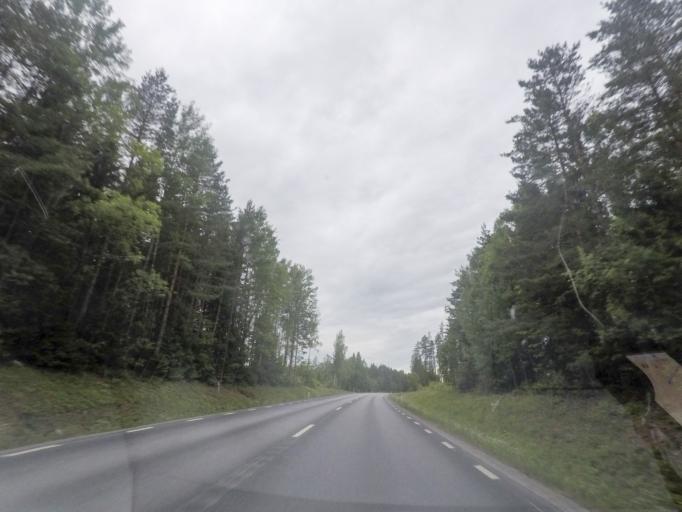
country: SE
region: OErebro
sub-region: Lindesbergs Kommun
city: Lindesberg
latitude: 59.5376
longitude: 15.2557
